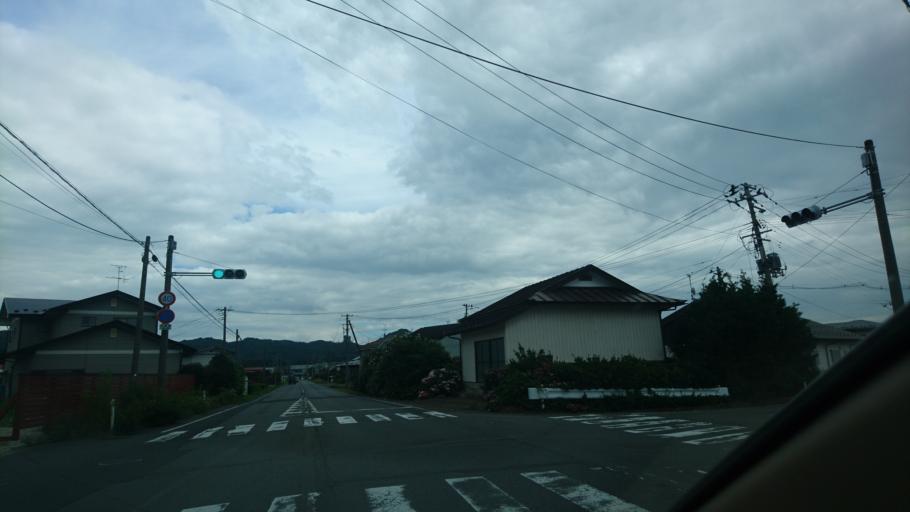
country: JP
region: Iwate
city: Kitakami
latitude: 39.2733
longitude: 141.1122
